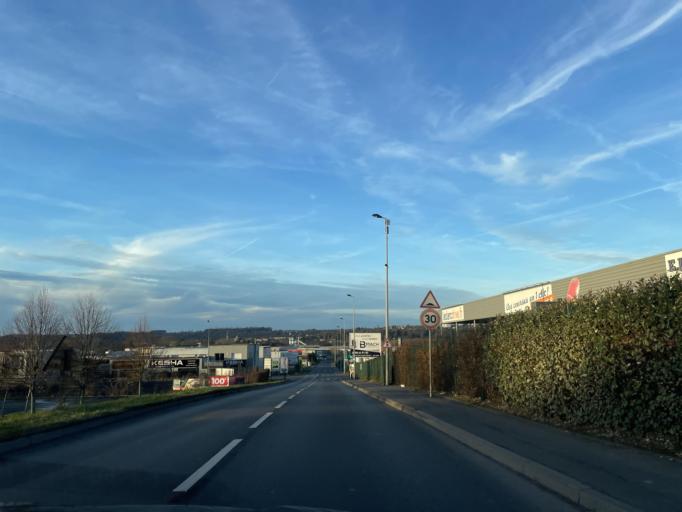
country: FR
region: Ile-de-France
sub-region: Departement de Seine-et-Marne
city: Coulommiers
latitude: 48.8014
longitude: 3.0979
